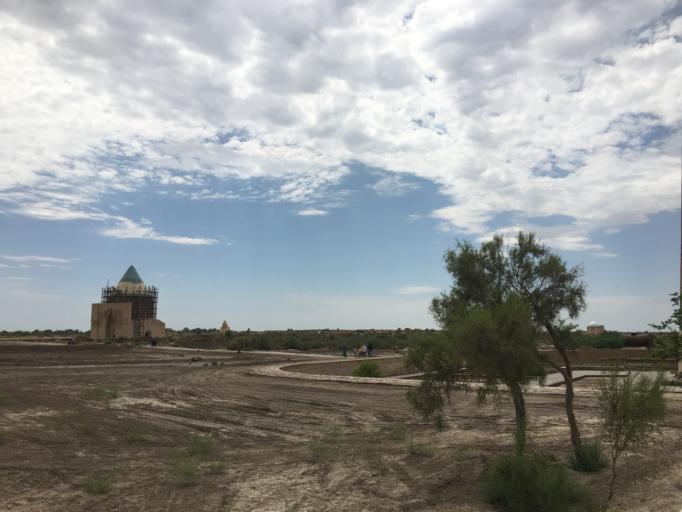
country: TM
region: Dasoguz
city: Koeneuergench
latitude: 42.3091
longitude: 59.1420
